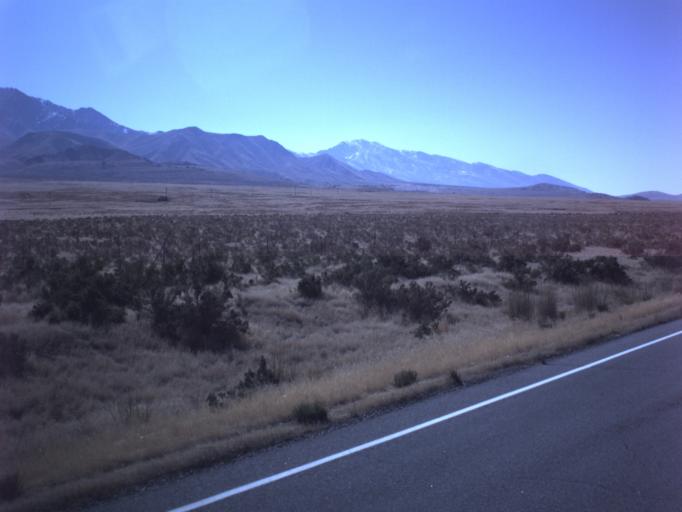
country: US
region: Utah
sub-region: Tooele County
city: Grantsville
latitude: 40.6572
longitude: -112.6808
